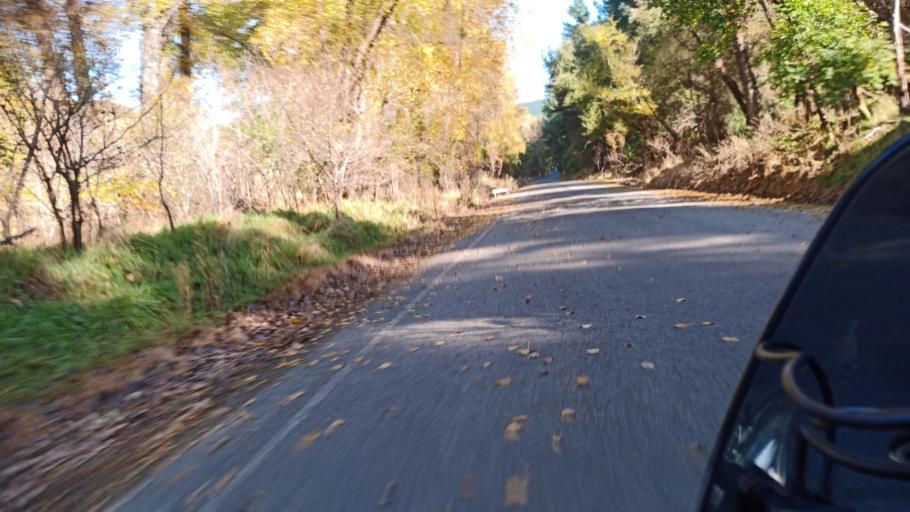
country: NZ
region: Hawke's Bay
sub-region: Wairoa District
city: Wairoa
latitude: -38.9204
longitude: 177.2506
